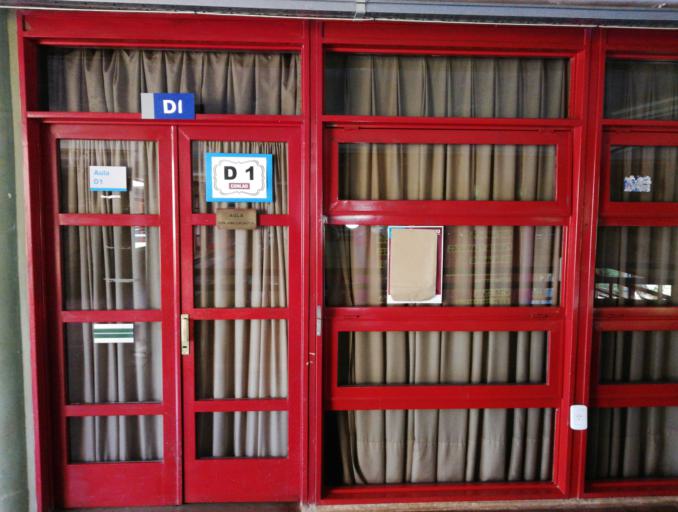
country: AR
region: Misiones
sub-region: Departamento de Capital
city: Posadas
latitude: -27.4345
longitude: -55.8878
